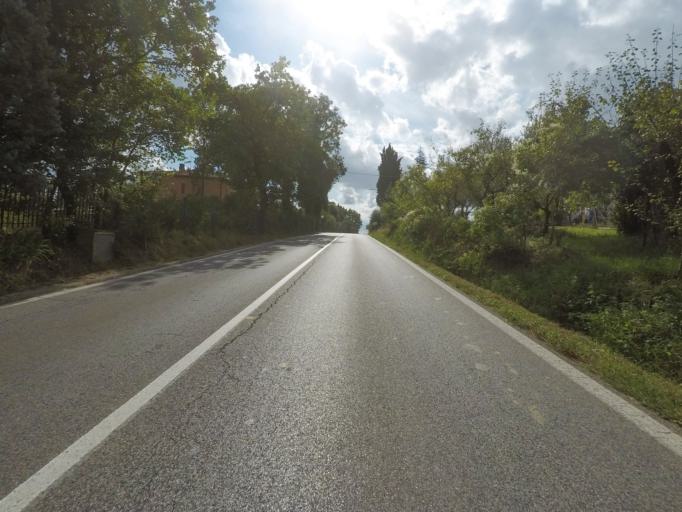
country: IT
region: Tuscany
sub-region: Provincia di Siena
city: Torrita di Siena
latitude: 43.1758
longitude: 11.7731
